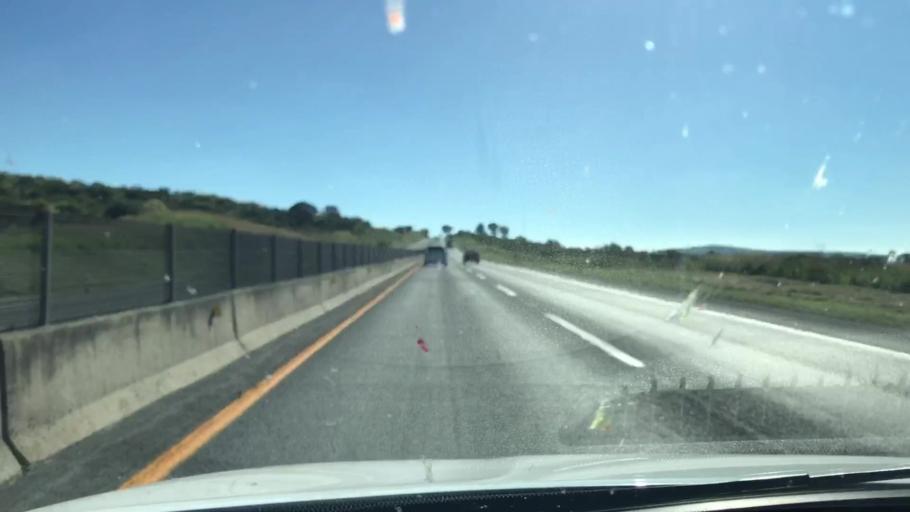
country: MX
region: Jalisco
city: Valle de Guadalupe
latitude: 20.9692
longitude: -102.6236
